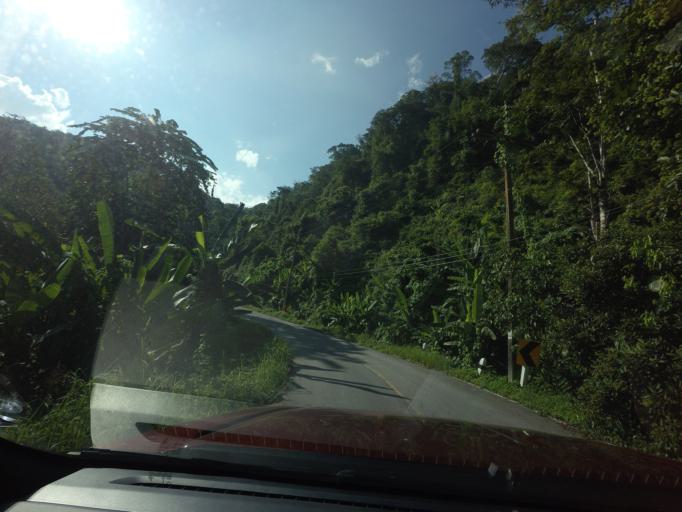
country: TH
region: Yala
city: Than To
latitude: 6.0871
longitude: 101.3286
